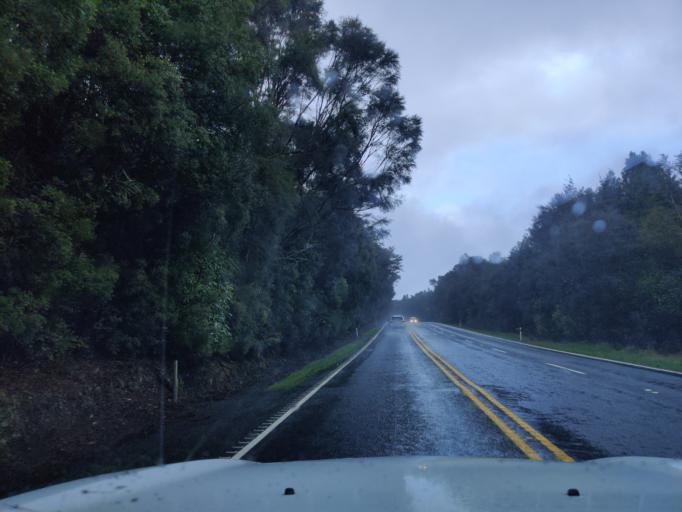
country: NZ
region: Waikato
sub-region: South Waikato District
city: Tokoroa
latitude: -38.0202
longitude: 175.9557
